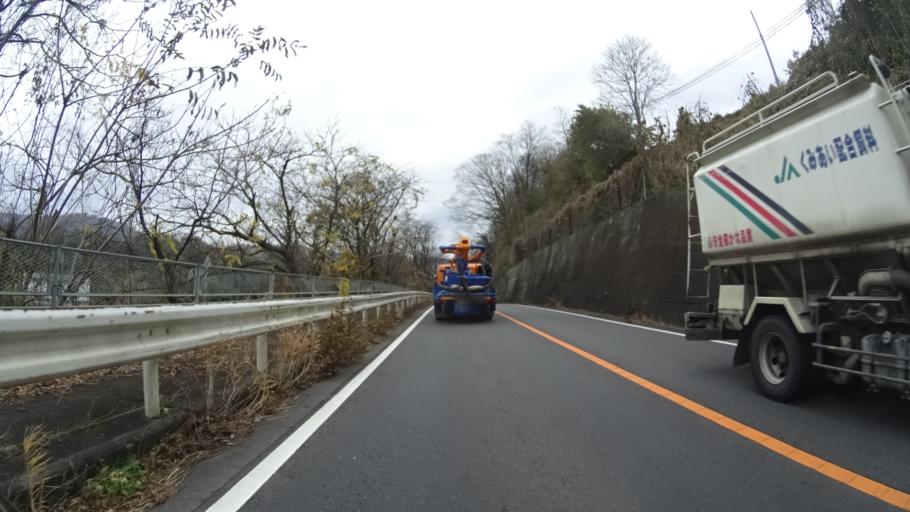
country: JP
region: Gunma
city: Numata
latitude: 36.6084
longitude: 139.0432
